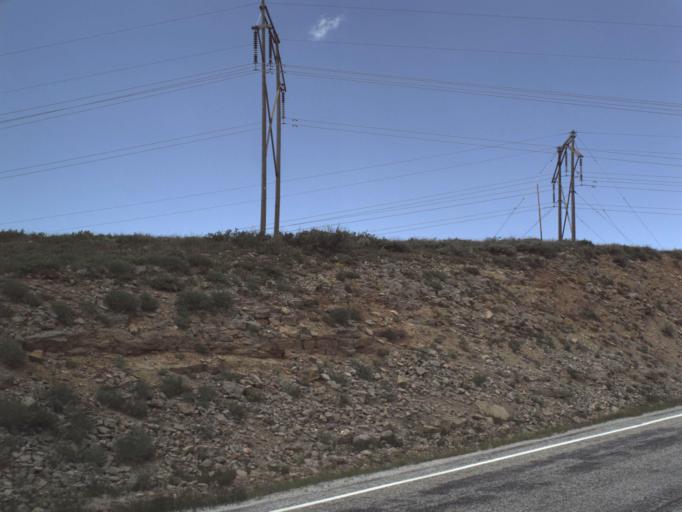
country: US
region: Utah
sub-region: Weber County
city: Wolf Creek
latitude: 41.4083
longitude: -111.5240
